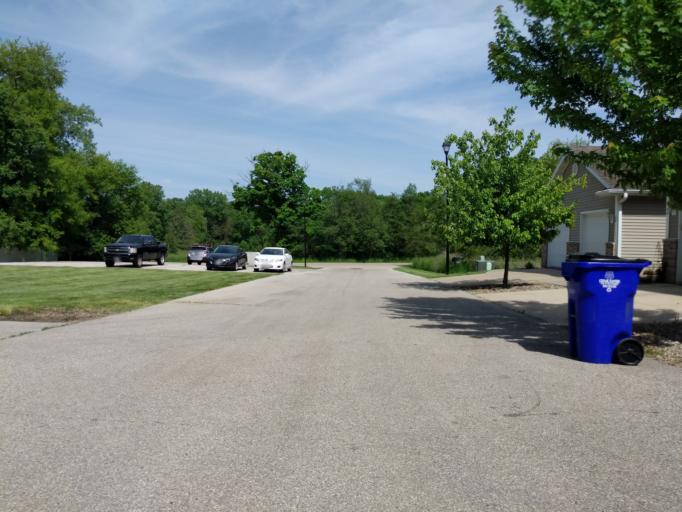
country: US
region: Iowa
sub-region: Linn County
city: Cedar Rapids
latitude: 42.0161
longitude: -91.6317
